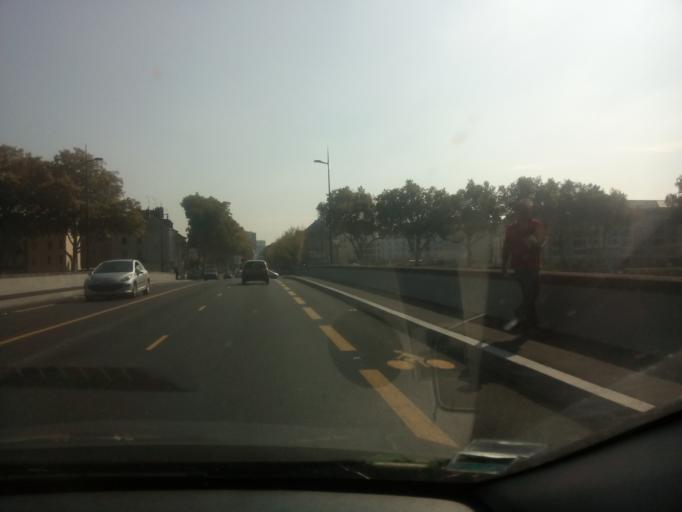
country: FR
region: Pays de la Loire
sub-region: Departement de Maine-et-Loire
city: Angers
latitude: 47.4780
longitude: -0.5549
